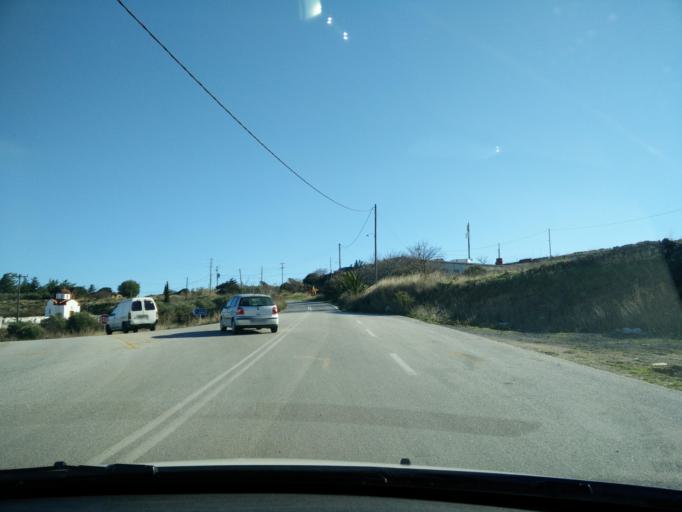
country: GR
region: Crete
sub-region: Nomos Irakleiou
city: Arkalochori
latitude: 35.1348
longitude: 25.2648
